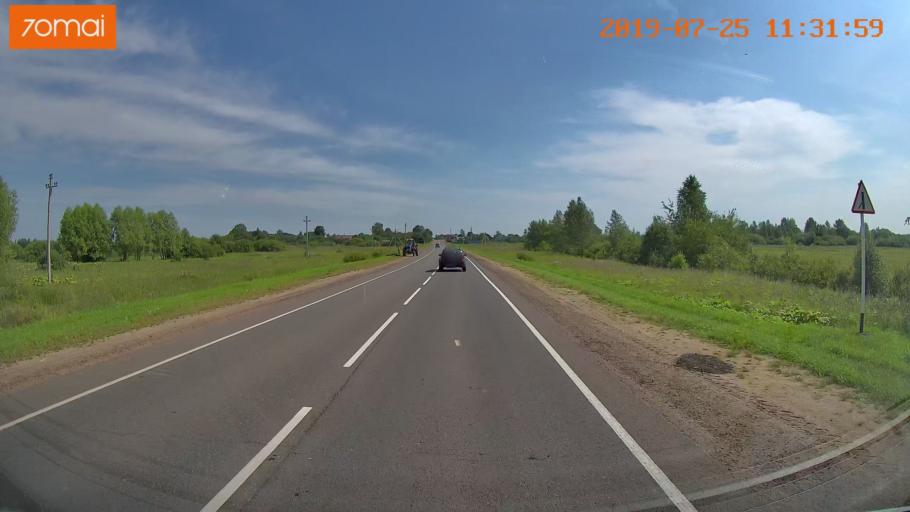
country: RU
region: Ivanovo
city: Privolzhsk
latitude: 57.3879
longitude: 41.3582
